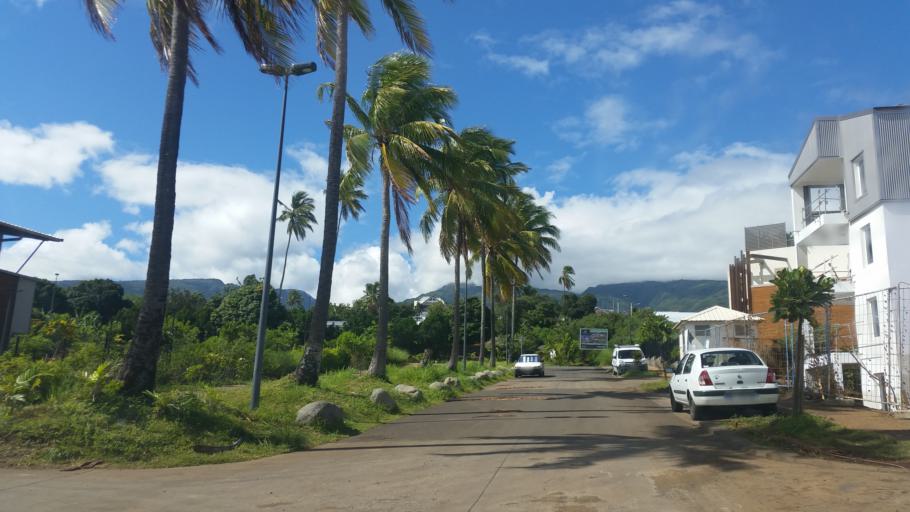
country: RE
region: Reunion
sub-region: Reunion
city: Sainte-Marie
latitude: -20.9076
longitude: 55.5005
